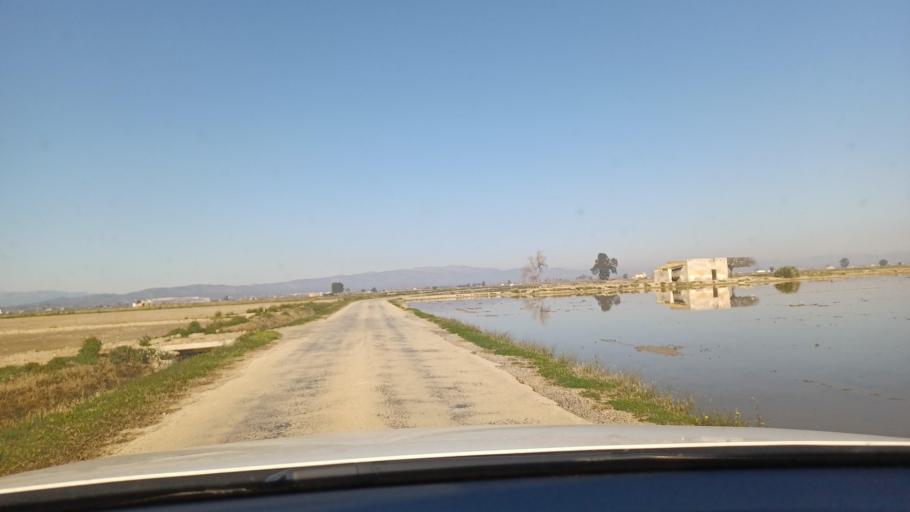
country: ES
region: Catalonia
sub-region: Provincia de Tarragona
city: Deltebre
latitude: 40.6894
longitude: 0.6517
